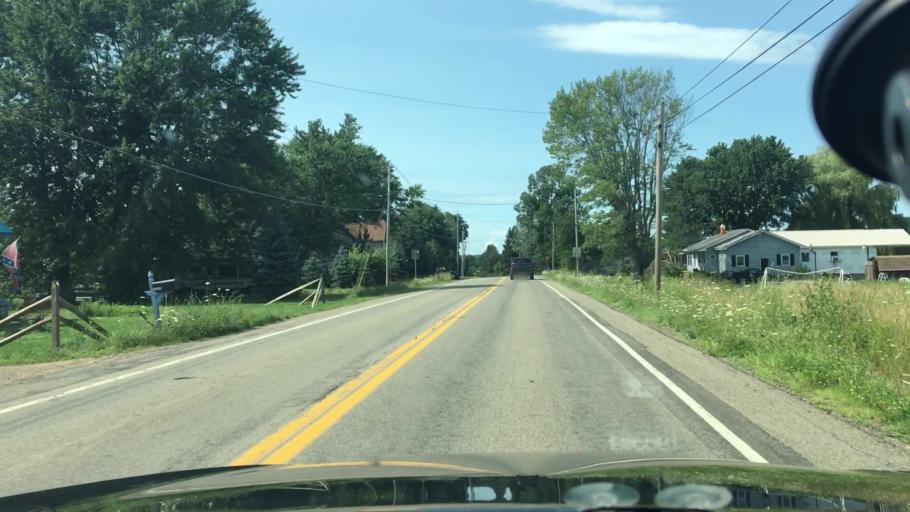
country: US
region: New York
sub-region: Chautauqua County
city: Brocton
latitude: 42.2653
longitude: -79.3500
